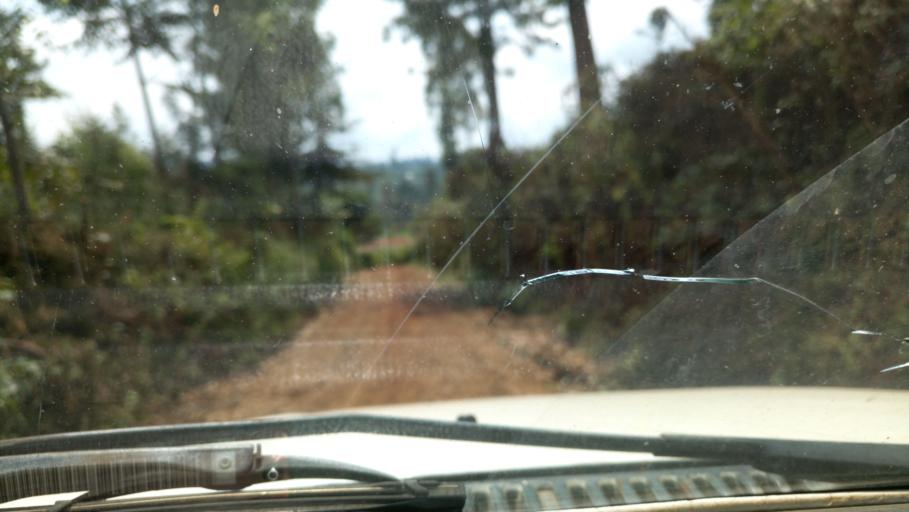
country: KE
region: Nyeri
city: Othaya
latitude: -0.5903
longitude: 37.0069
